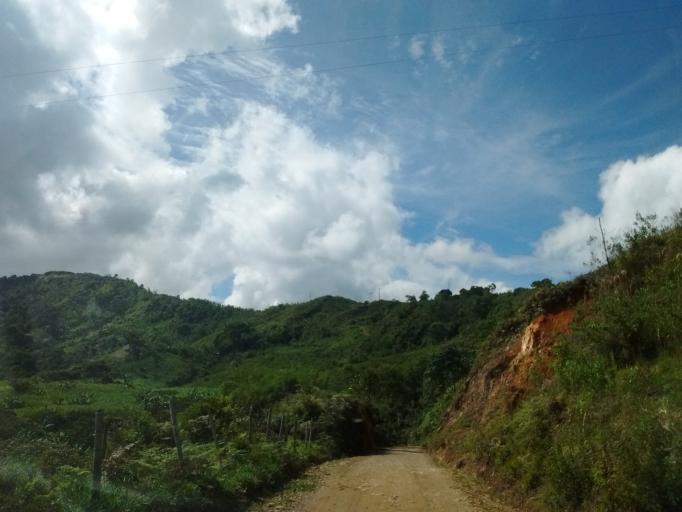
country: CO
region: Cauca
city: Morales
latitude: 2.6911
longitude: -76.7431
